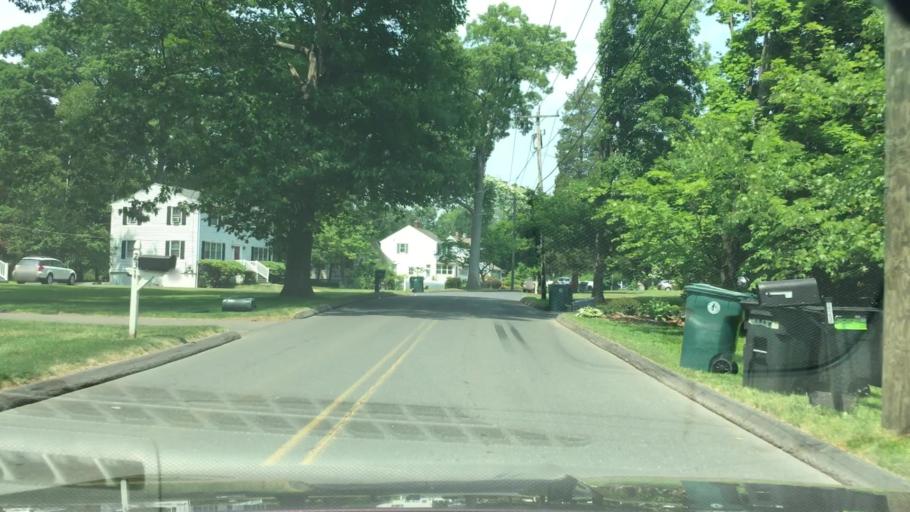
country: US
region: Connecticut
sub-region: New Haven County
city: Cheshire Village
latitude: 41.5158
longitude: -72.9181
